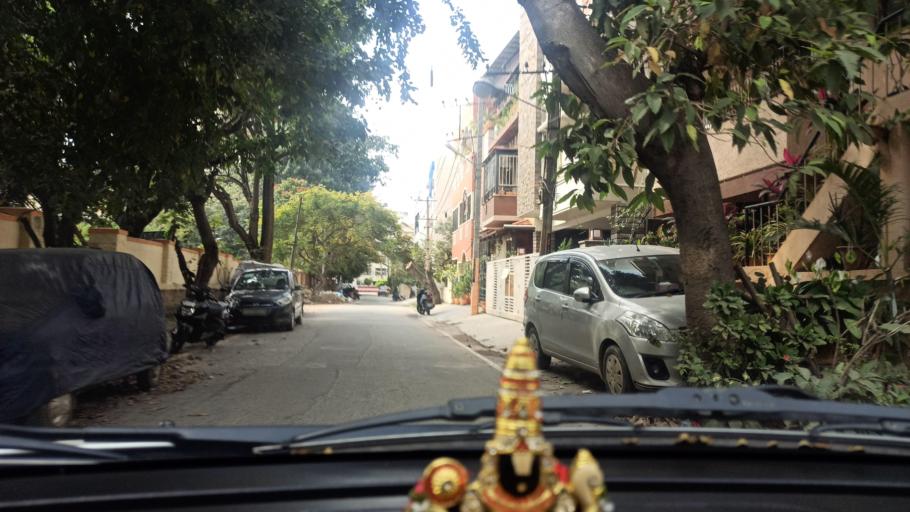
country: IN
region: Karnataka
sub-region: Bangalore Urban
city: Bangalore
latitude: 13.0124
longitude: 77.6563
